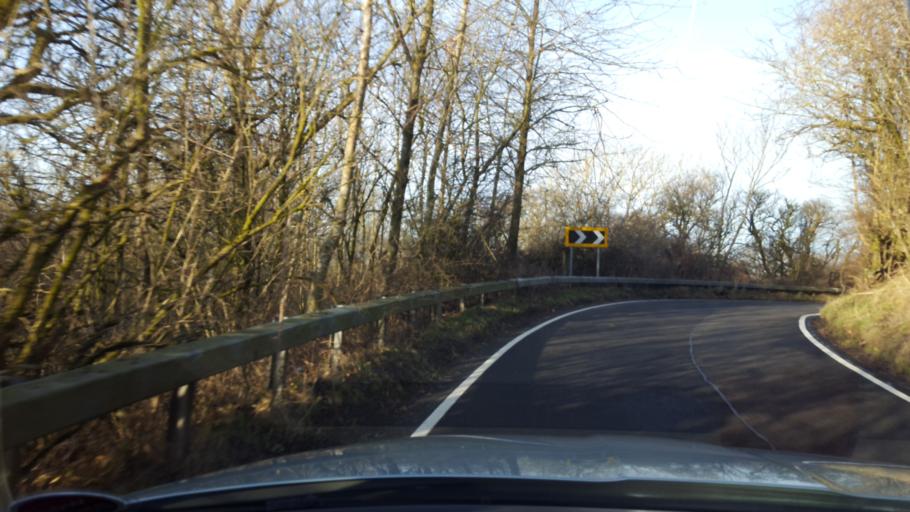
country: GB
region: Scotland
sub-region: West Lothian
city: Livingston
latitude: 55.8549
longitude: -3.5143
